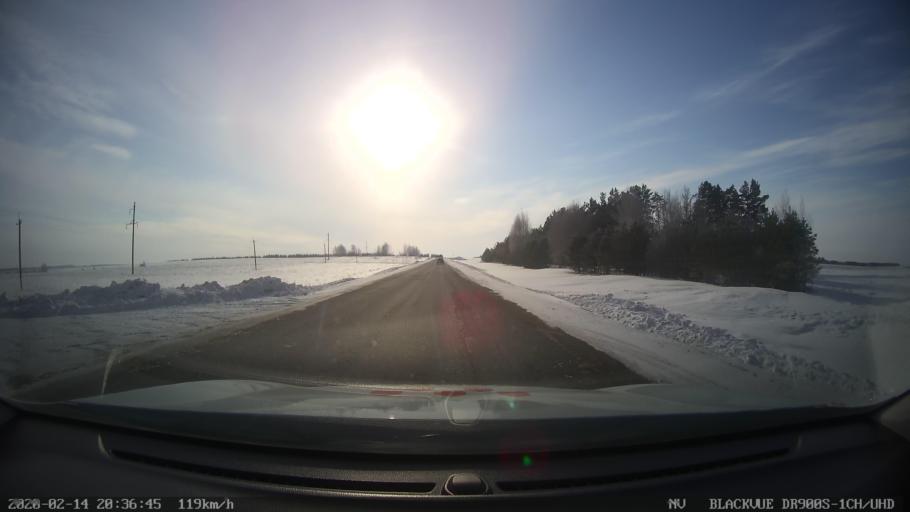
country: RU
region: Tatarstan
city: Kuybyshevskiy Zaton
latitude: 55.3620
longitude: 49.0023
